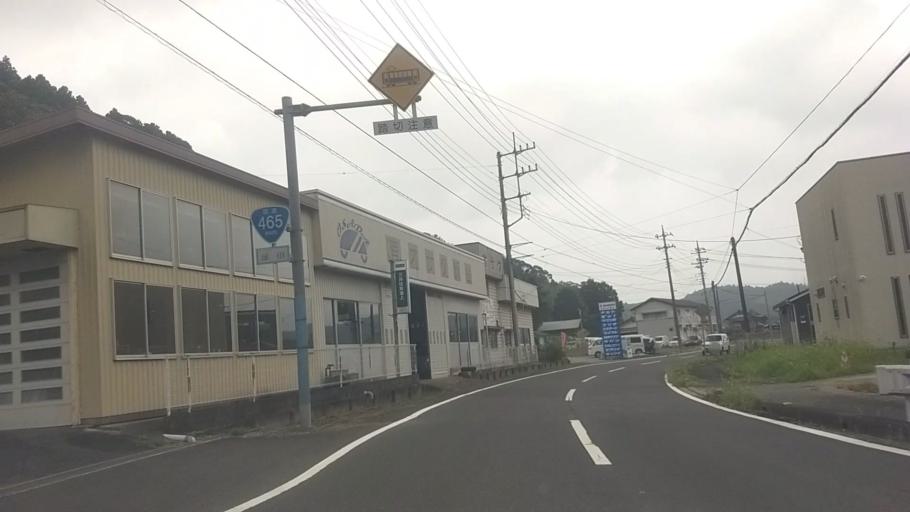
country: JP
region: Chiba
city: Ohara
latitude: 35.2621
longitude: 140.2509
